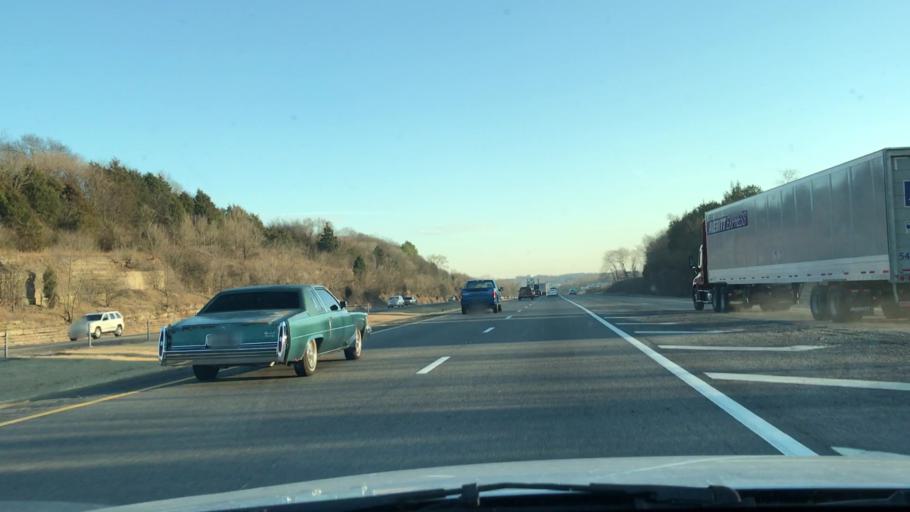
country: US
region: Tennessee
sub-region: Davidson County
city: Goodlettsville
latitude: 36.3447
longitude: -86.7155
